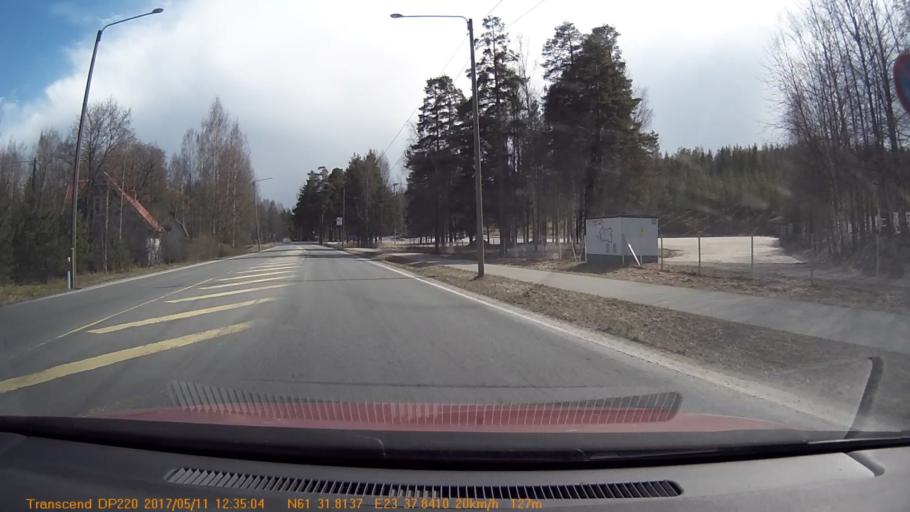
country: FI
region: Pirkanmaa
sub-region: Tampere
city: Yloejaervi
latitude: 61.5303
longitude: 23.6306
